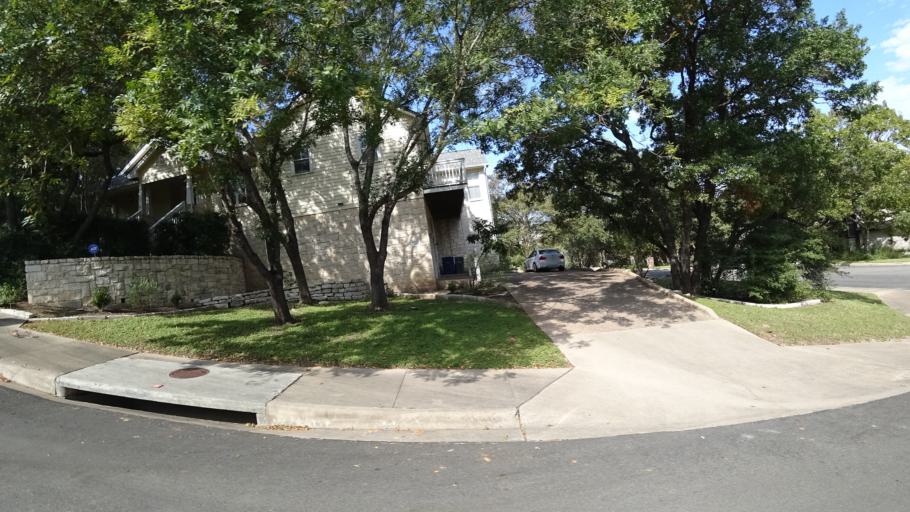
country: US
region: Texas
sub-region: Travis County
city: West Lake Hills
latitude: 30.3495
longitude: -97.7685
